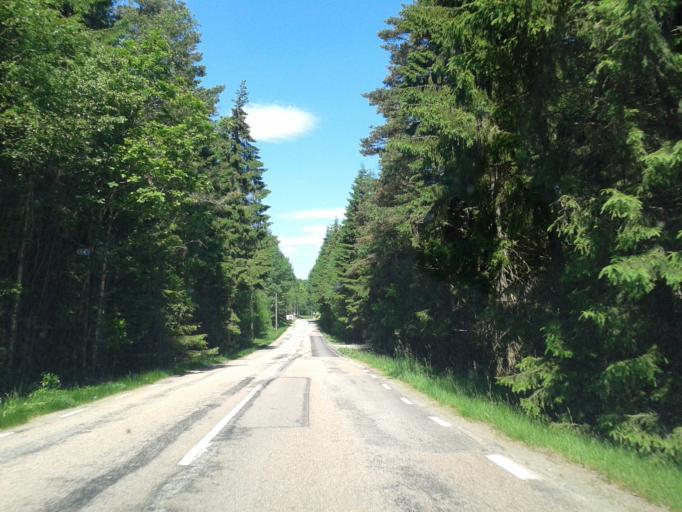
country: SE
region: Vaestra Goetaland
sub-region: Orust
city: Henan
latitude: 58.2783
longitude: 11.7178
